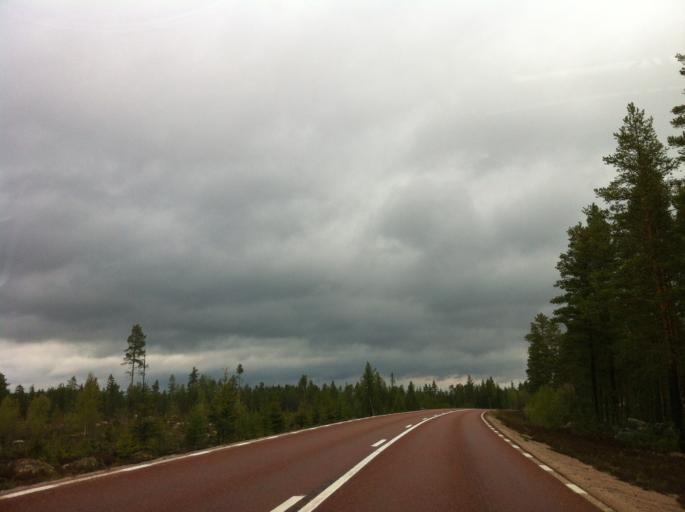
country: SE
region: Jaemtland
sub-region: Harjedalens Kommun
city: Sveg
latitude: 61.9037
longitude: 14.6215
